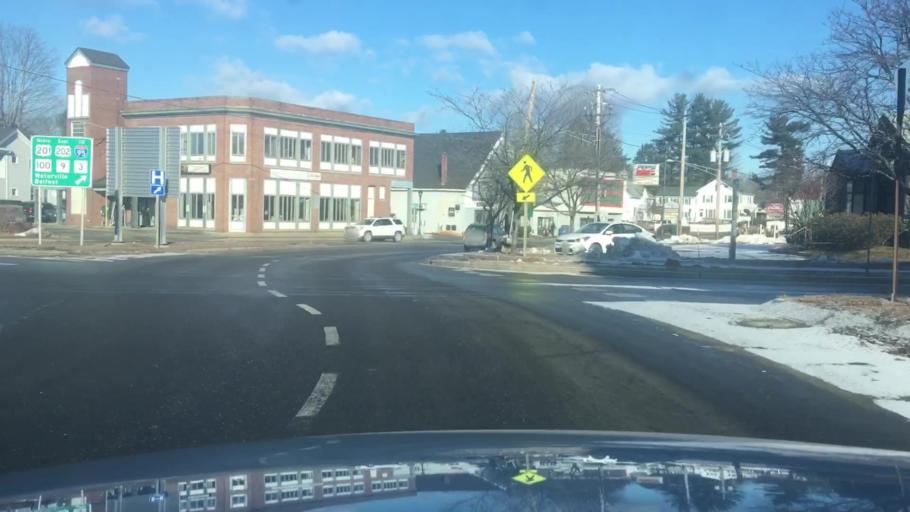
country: US
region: Maine
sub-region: Kennebec County
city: Augusta
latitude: 44.3164
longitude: -69.7676
